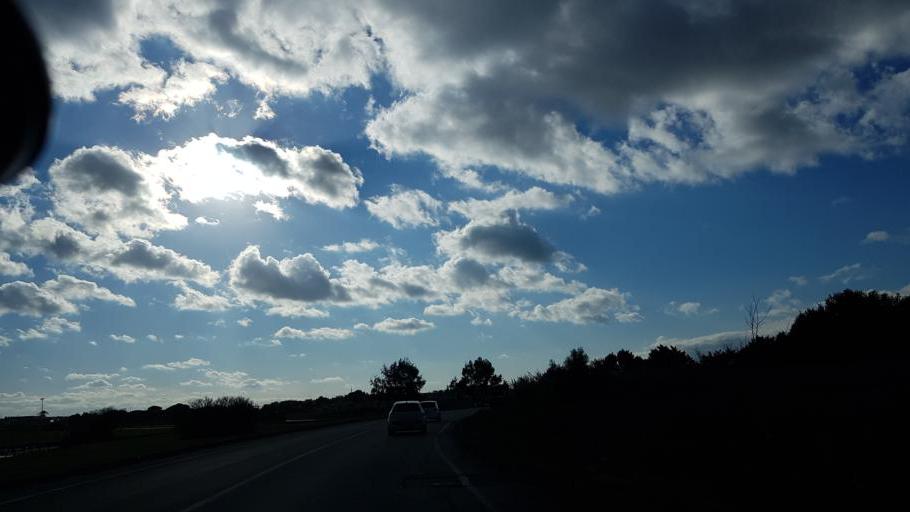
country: IT
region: Apulia
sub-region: Provincia di Brindisi
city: Brindisi
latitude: 40.6521
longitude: 17.9328
